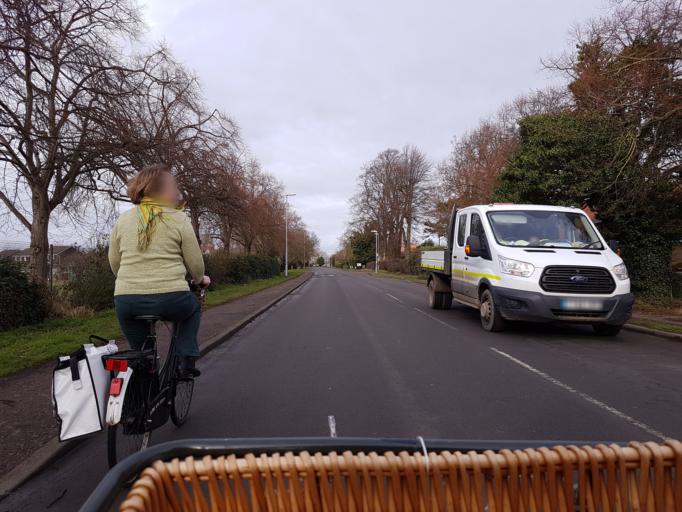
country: GB
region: England
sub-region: Cambridgeshire
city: Girton
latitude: 52.2355
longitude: 0.0859
